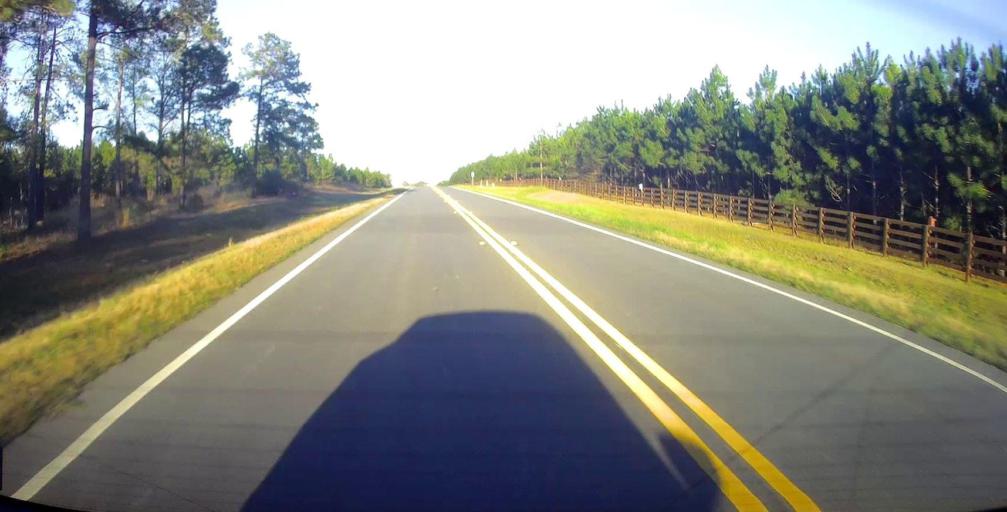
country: US
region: Georgia
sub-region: Wilcox County
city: Abbeville
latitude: 31.9878
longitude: -83.3332
